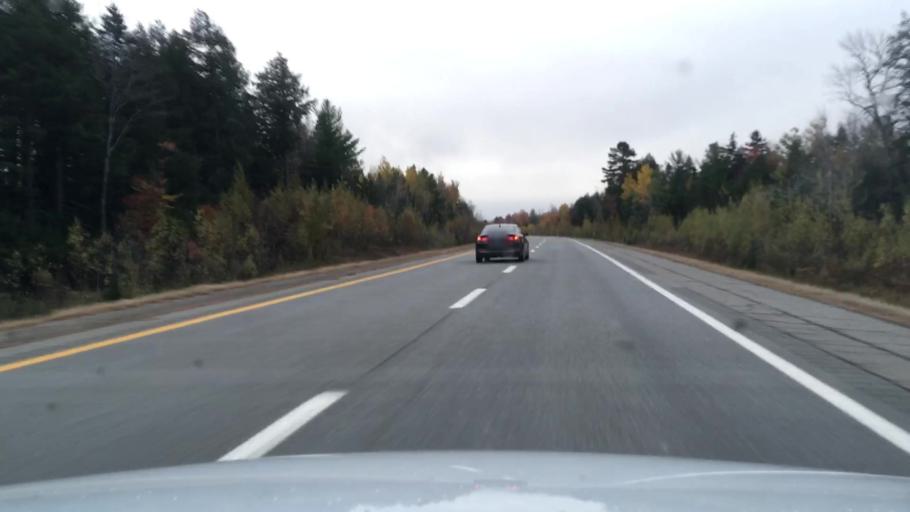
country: US
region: Maine
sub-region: Penobscot County
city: Greenbush
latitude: 45.1020
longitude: -68.6961
